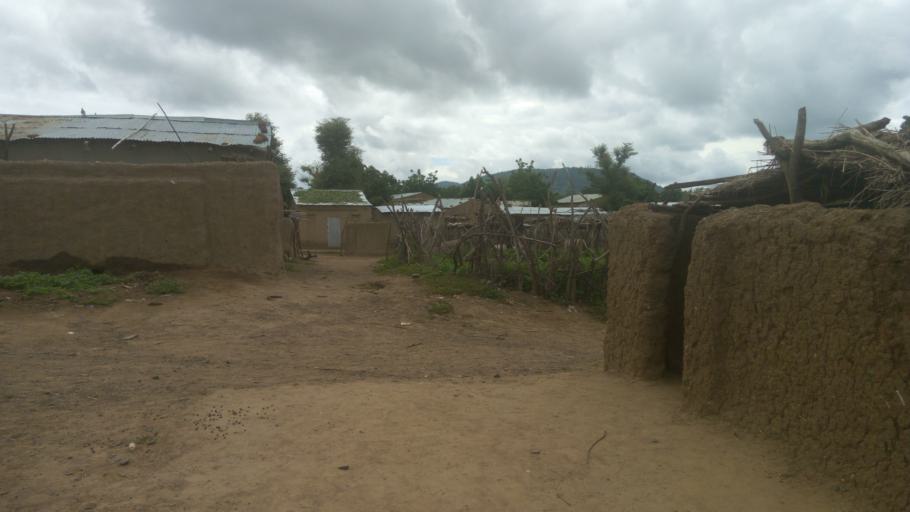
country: ML
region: Kayes
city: Yelimane
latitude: 14.6453
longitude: -10.7003
